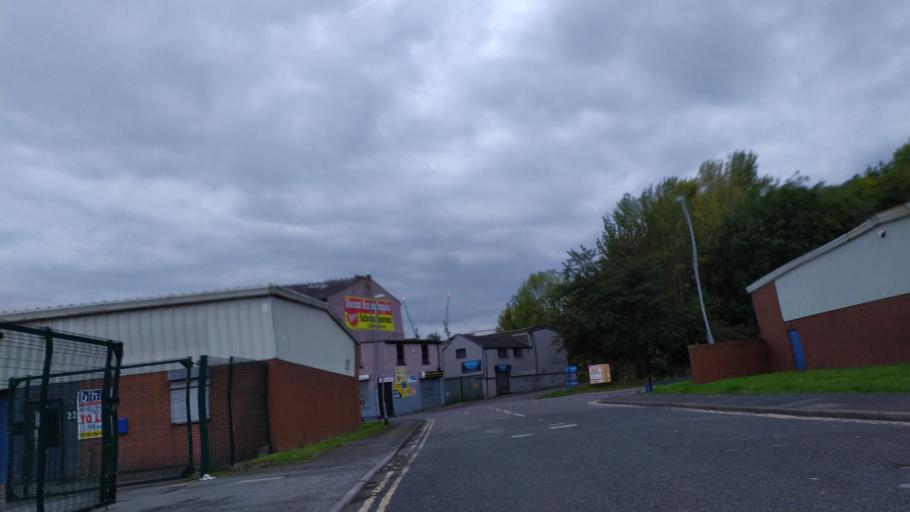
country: GB
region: England
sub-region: City and Borough of Leeds
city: Leeds
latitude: 53.8123
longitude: -1.5421
